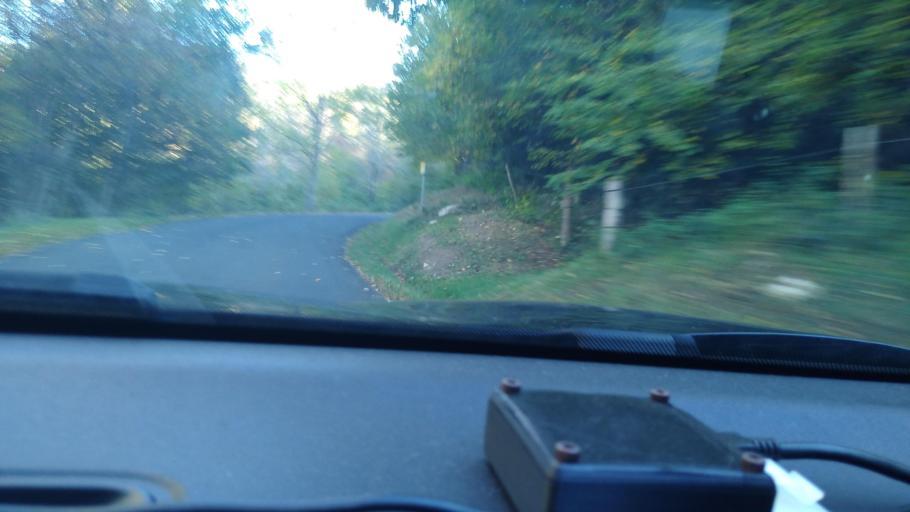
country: FR
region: Languedoc-Roussillon
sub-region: Departement de l'Aude
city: Quillan
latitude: 42.7351
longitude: 2.1396
